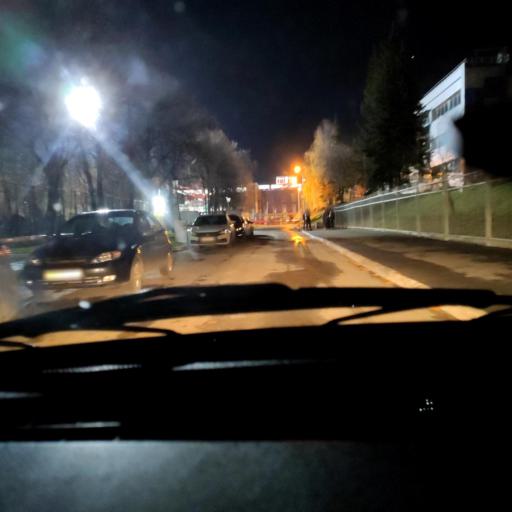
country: RU
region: Bashkortostan
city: Ufa
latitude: 54.8259
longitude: 56.0574
